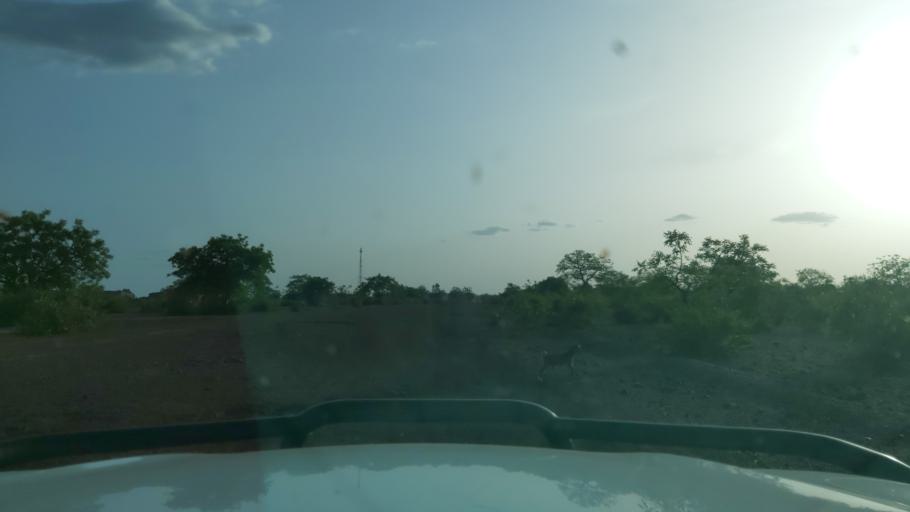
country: ML
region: Koulikoro
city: Kolokani
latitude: 13.2043
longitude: -7.9244
